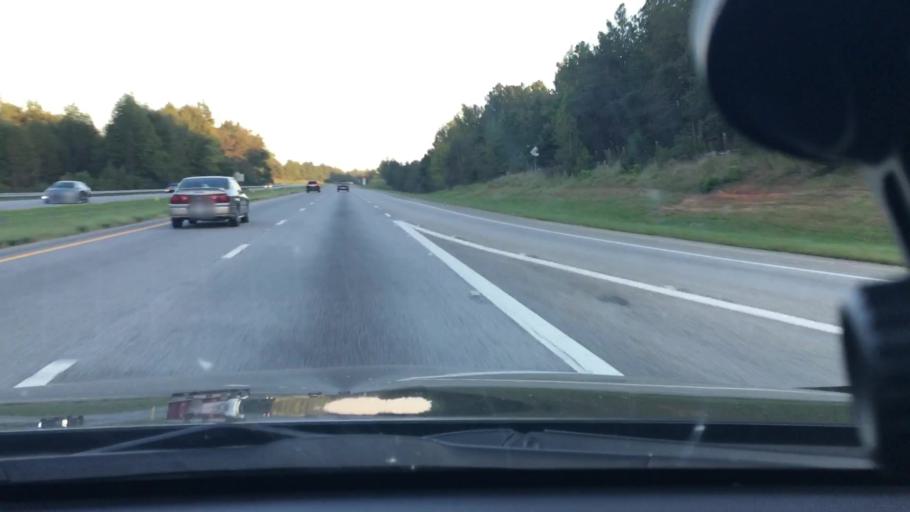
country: US
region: South Carolina
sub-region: Spartanburg County
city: Inman
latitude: 35.0793
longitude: -82.0606
